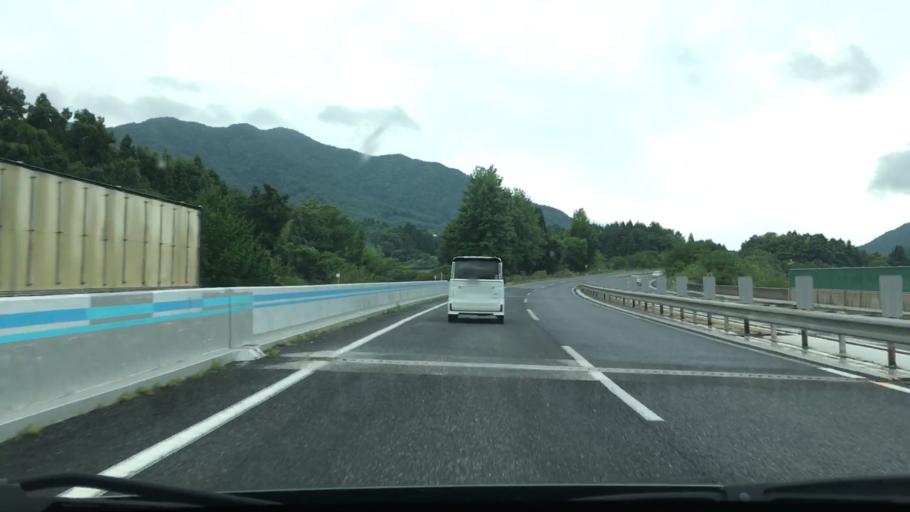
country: JP
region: Hiroshima
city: Hiroshima-shi
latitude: 34.6434
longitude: 132.5172
